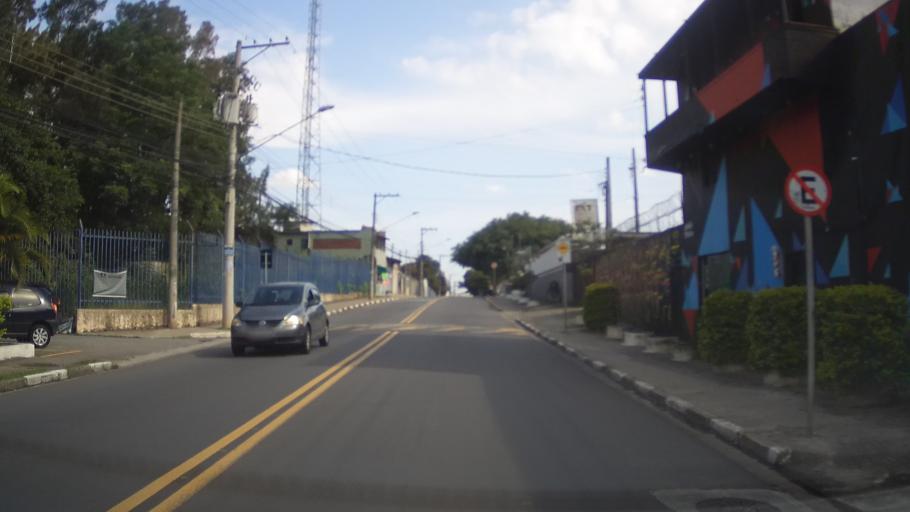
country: BR
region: Sao Paulo
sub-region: Guarulhos
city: Guarulhos
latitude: -23.4596
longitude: -46.5011
